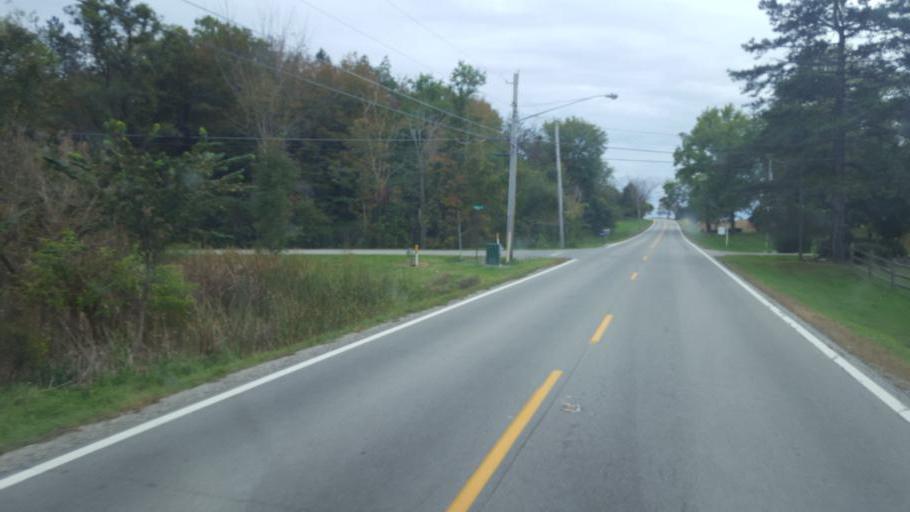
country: US
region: Ohio
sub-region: Huron County
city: Wakeman
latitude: 41.3062
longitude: -82.3686
